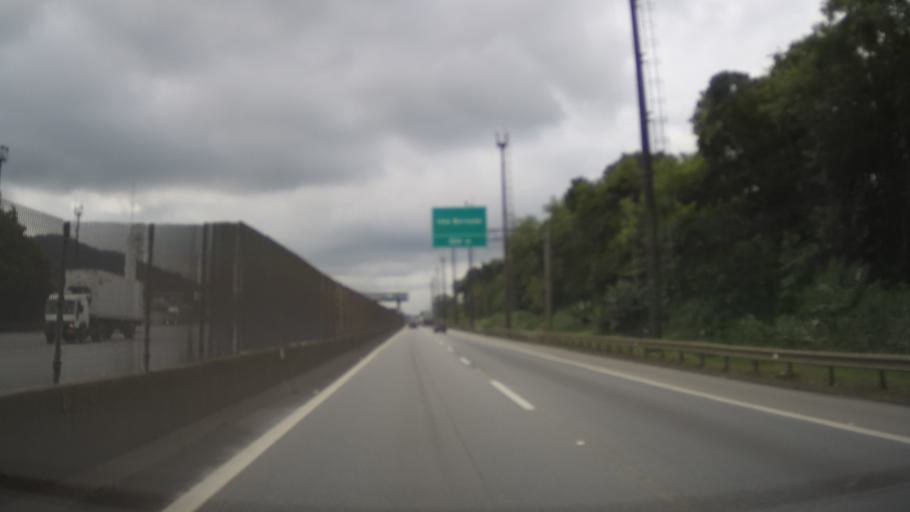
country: BR
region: Sao Paulo
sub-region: Santos
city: Santos
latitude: -23.8932
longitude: -46.3039
